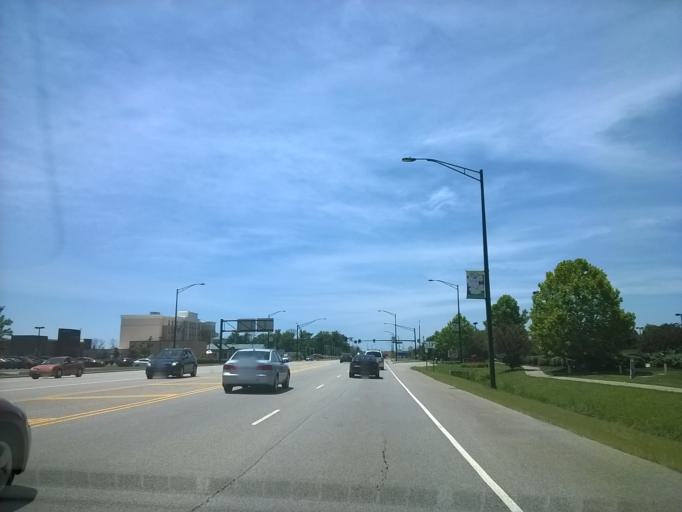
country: US
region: Ohio
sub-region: Butler County
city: Beckett Ridge
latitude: 39.3235
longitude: -84.4283
